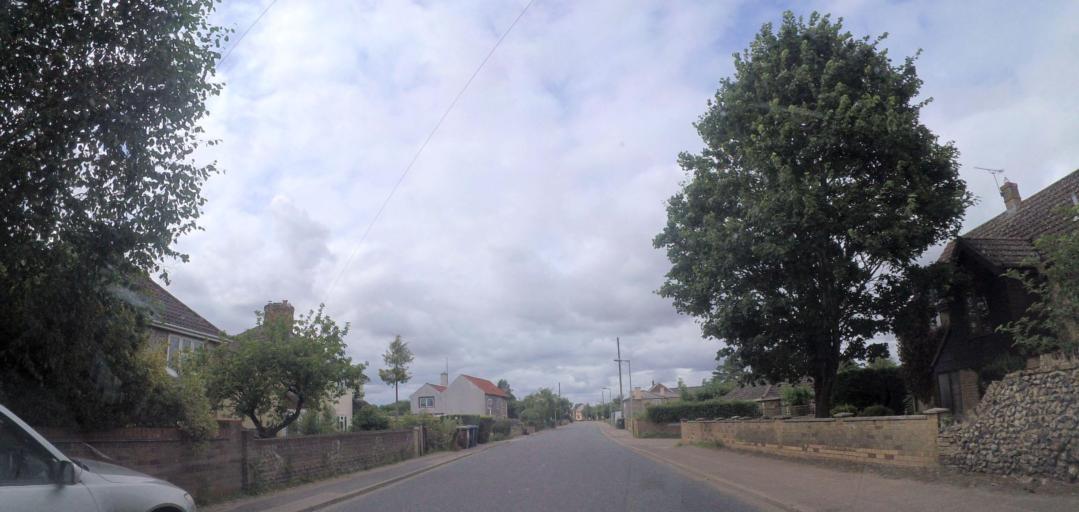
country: GB
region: England
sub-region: Suffolk
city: Lakenheath
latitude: 52.3129
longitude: 0.5478
